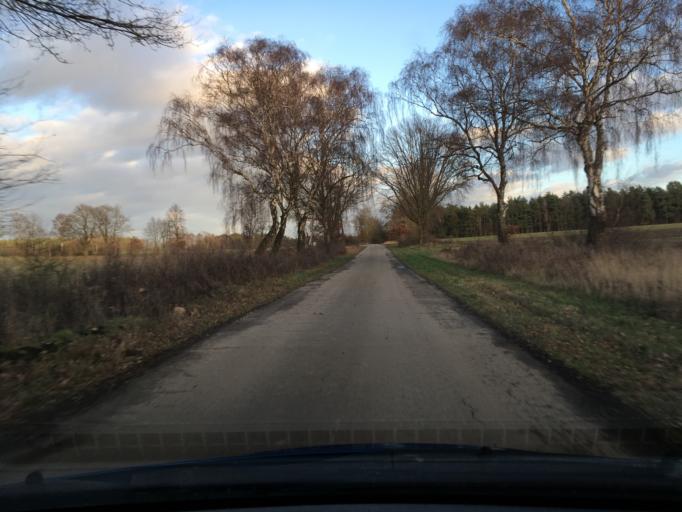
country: DE
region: Lower Saxony
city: Soderstorf
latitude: 53.1152
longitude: 10.1657
